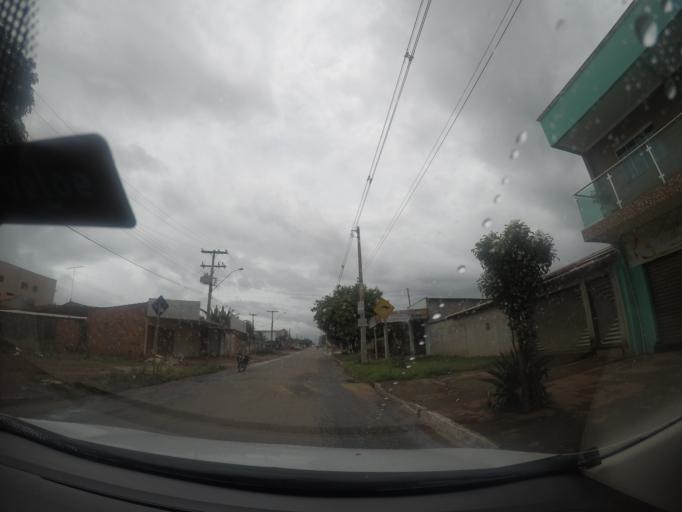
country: BR
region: Goias
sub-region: Trindade
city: Trindade
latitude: -16.6424
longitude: -49.3875
